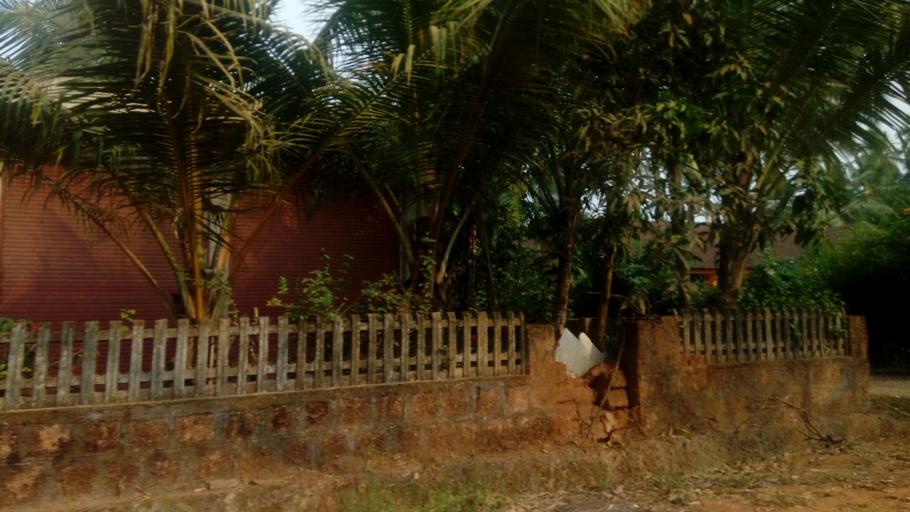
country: IN
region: Goa
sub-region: South Goa
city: Benaulim
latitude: 15.2531
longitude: 73.9339
